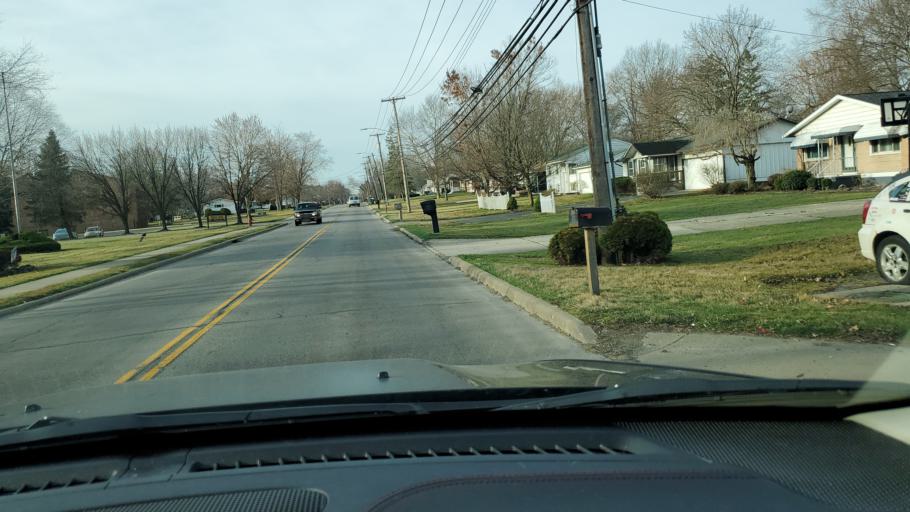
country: US
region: Ohio
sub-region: Trumbull County
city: Bolindale
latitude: 41.2081
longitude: -80.7643
